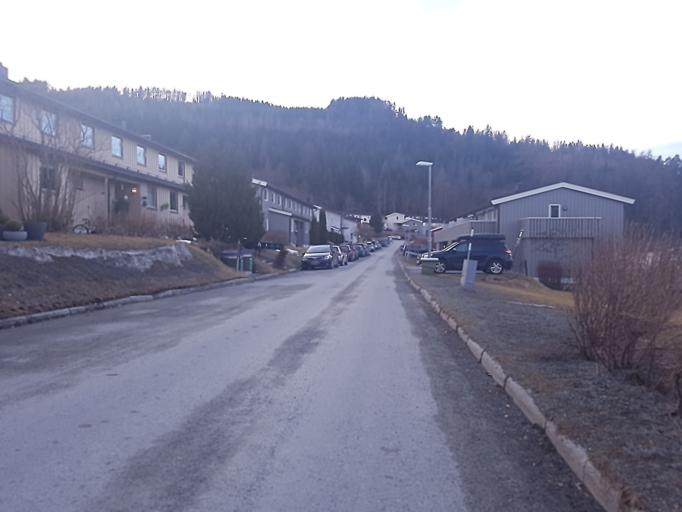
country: NO
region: Sor-Trondelag
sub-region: Trondheim
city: Trondheim
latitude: 63.4288
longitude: 10.3478
